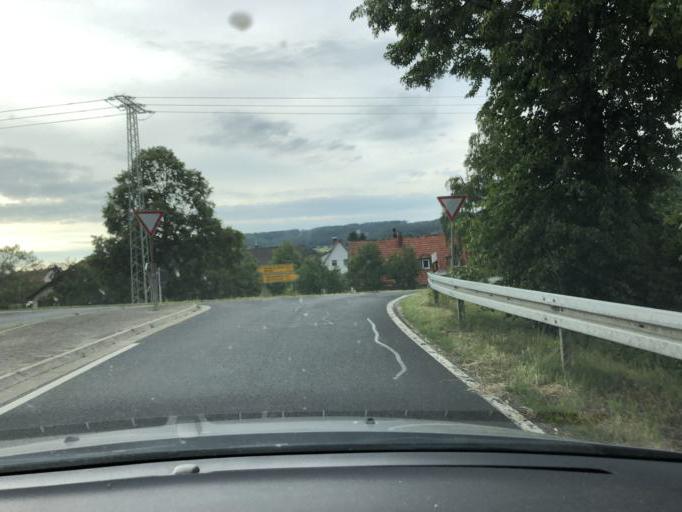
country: DE
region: Hesse
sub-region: Regierungsbezirk Kassel
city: Alheim
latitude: 51.0618
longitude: 9.6088
